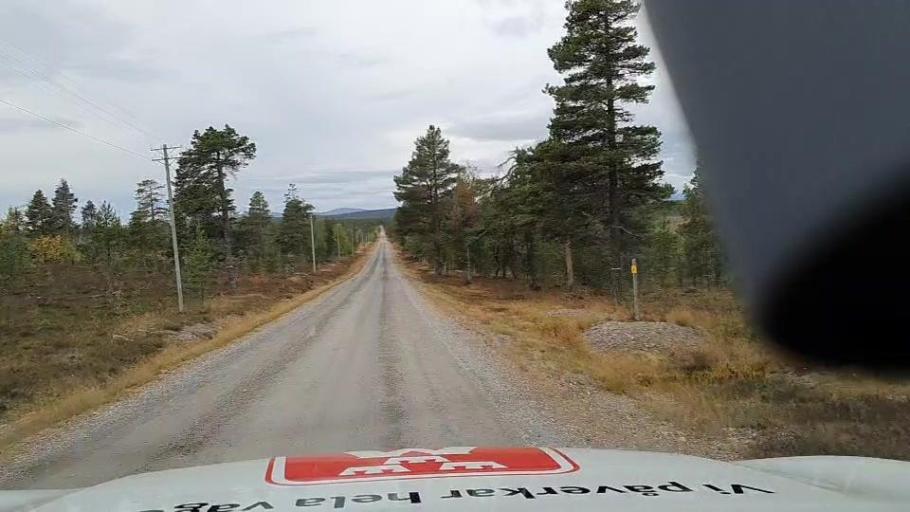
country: NO
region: Hedmark
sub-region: Engerdal
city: Engerdal
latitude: 62.0934
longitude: 12.8091
